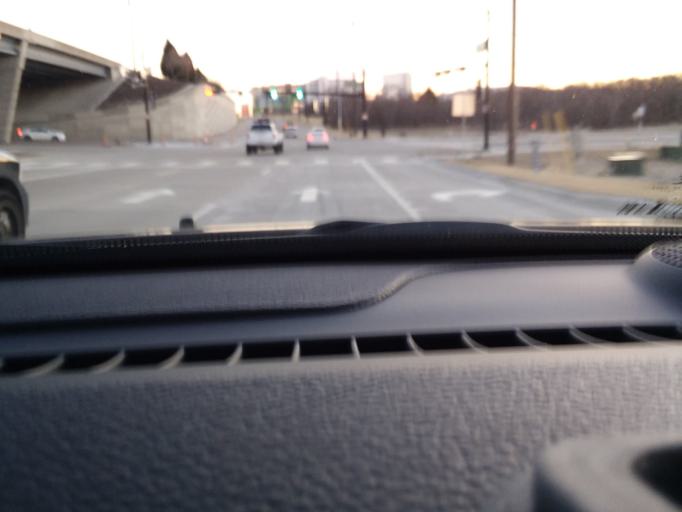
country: US
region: Texas
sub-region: Collin County
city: Frisco
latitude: 33.1168
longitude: -96.8233
